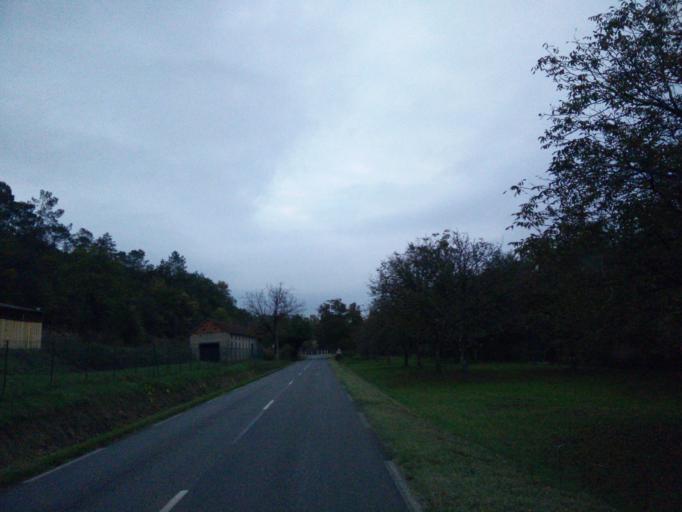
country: FR
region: Aquitaine
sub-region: Departement de la Dordogne
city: Carsac-Aillac
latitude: 44.7927
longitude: 1.3073
